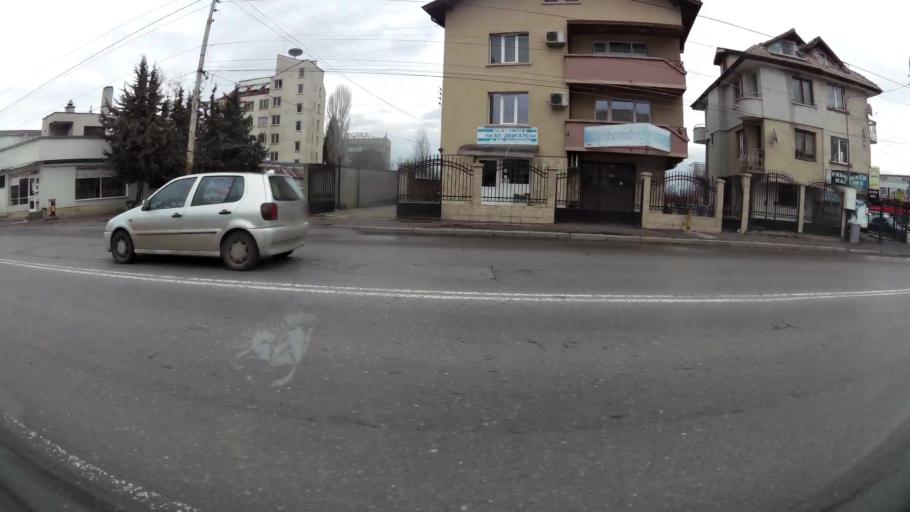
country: BG
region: Sofiya
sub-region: Obshtina Bozhurishte
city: Bozhurishte
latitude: 42.7315
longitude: 23.2536
